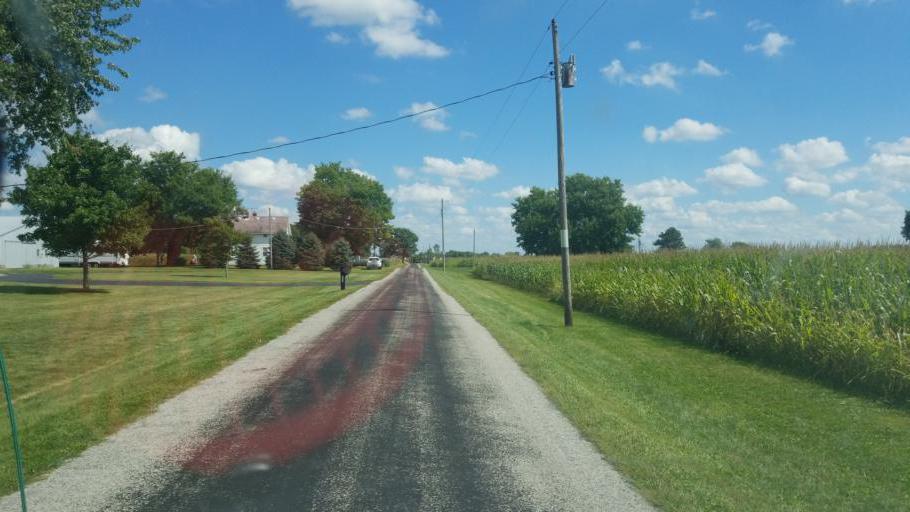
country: US
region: Ohio
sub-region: Marion County
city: Prospect
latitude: 40.3637
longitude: -83.2122
